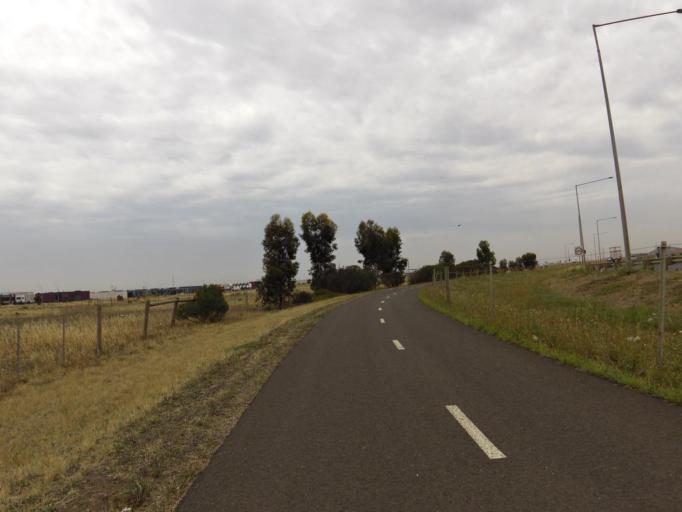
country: AU
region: Victoria
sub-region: Melton
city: Caroline Springs
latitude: -37.7595
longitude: 144.7406
